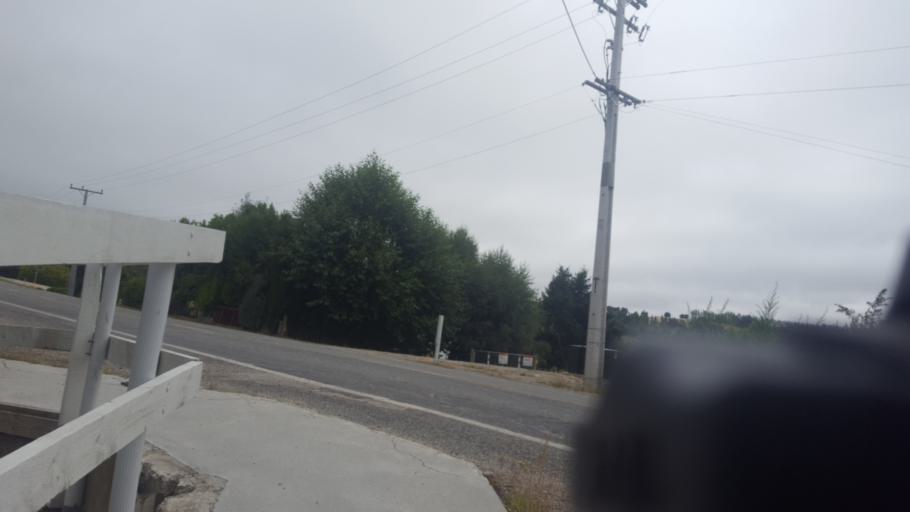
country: NZ
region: Otago
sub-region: Queenstown-Lakes District
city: Kingston
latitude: -45.5319
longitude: 169.2993
